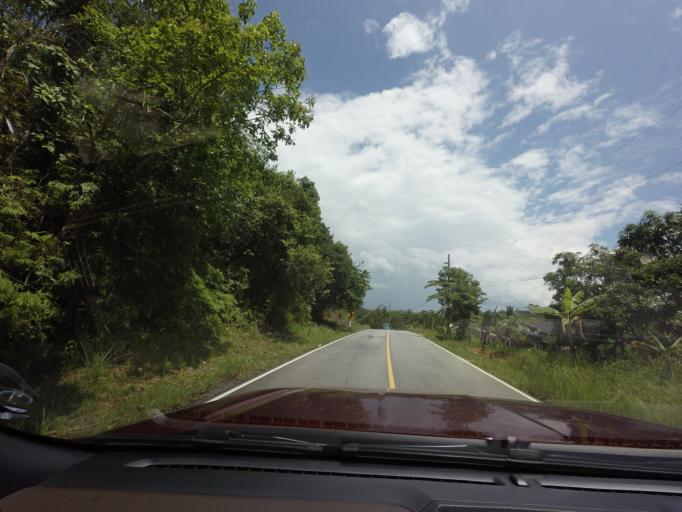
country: TH
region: Narathiwat
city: Chanae
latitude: 6.0775
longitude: 101.6881
